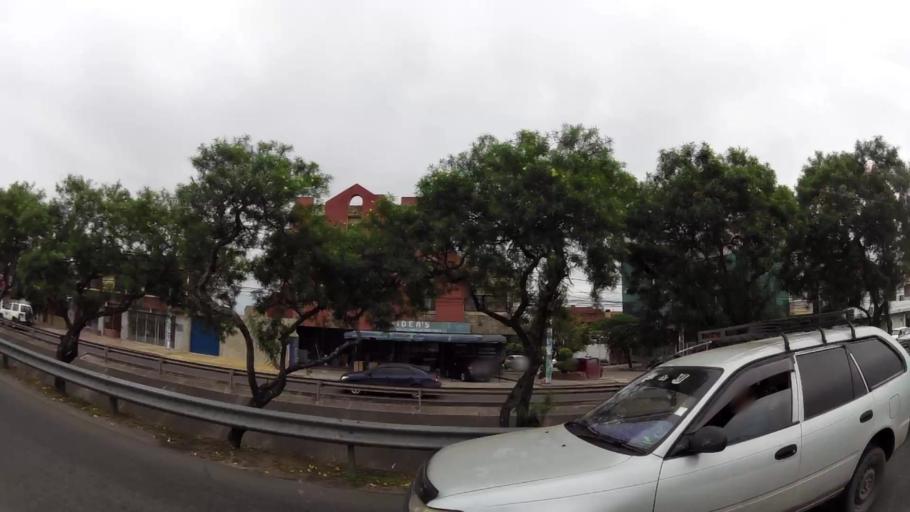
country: BO
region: Santa Cruz
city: Santa Cruz de la Sierra
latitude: -17.7829
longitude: -63.1948
